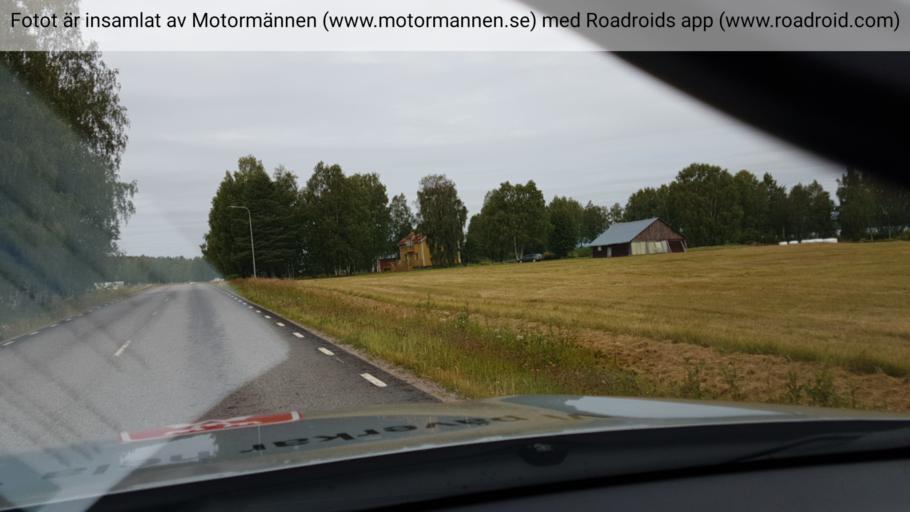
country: SE
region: Norrbotten
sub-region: Lulea Kommun
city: Sodra Sunderbyn
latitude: 65.6544
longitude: 21.8549
